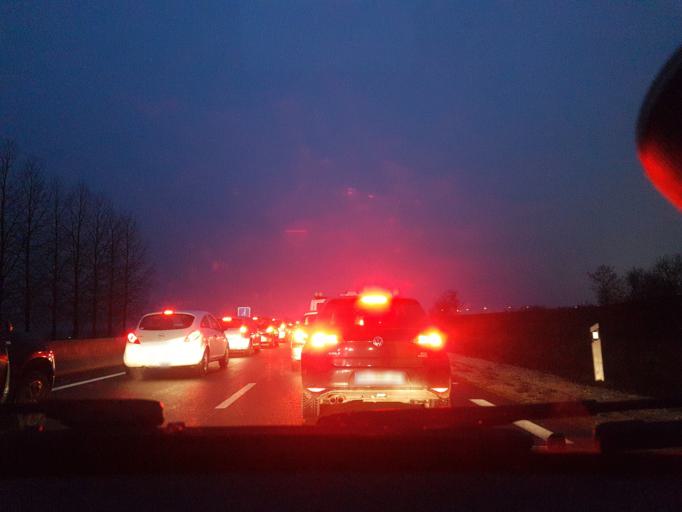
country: FR
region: Franche-Comte
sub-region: Departement du Doubs
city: Doubs
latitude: 46.9197
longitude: 6.3352
